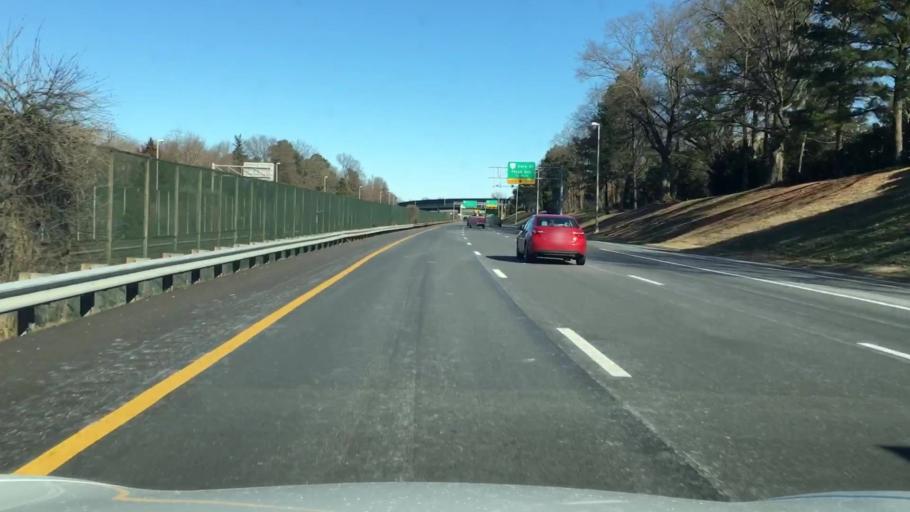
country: US
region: Virginia
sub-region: City of Richmond
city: Richmond
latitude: 37.5489
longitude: -77.4912
